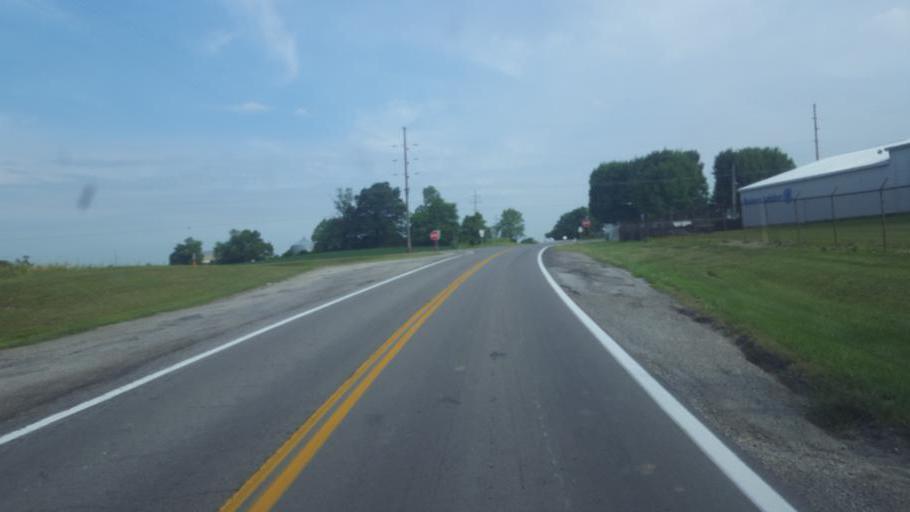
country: US
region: Ohio
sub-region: Marion County
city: Marion
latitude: 40.5486
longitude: -83.1913
